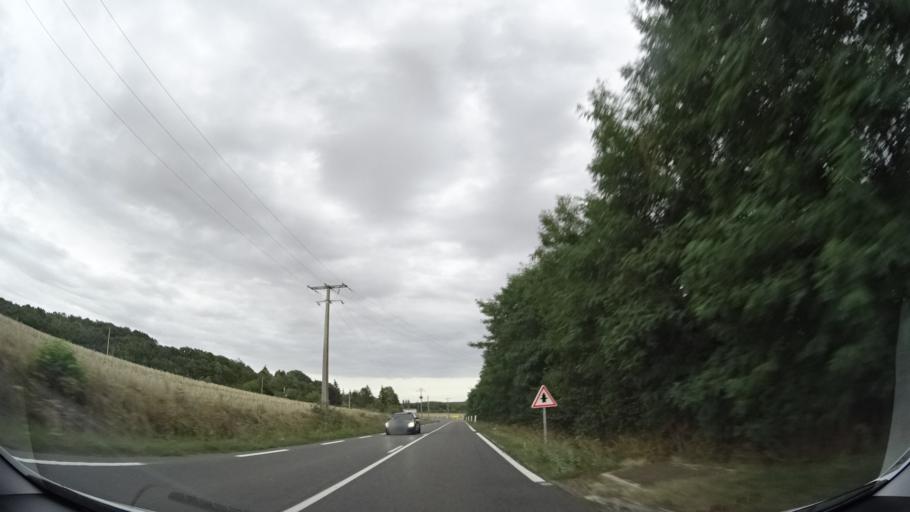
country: FR
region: Centre
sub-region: Departement du Loiret
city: Saint-Germain-des-Pres
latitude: 47.9364
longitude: 2.8918
